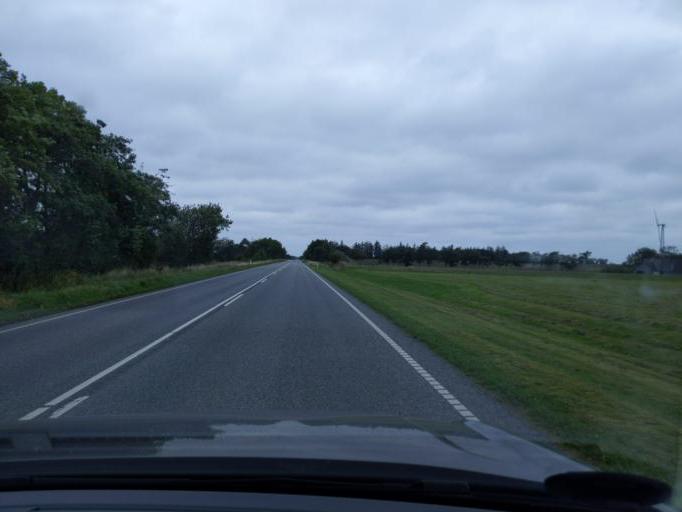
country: DK
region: Central Jutland
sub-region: Randers Kommune
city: Spentrup
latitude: 56.5237
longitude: 9.9318
